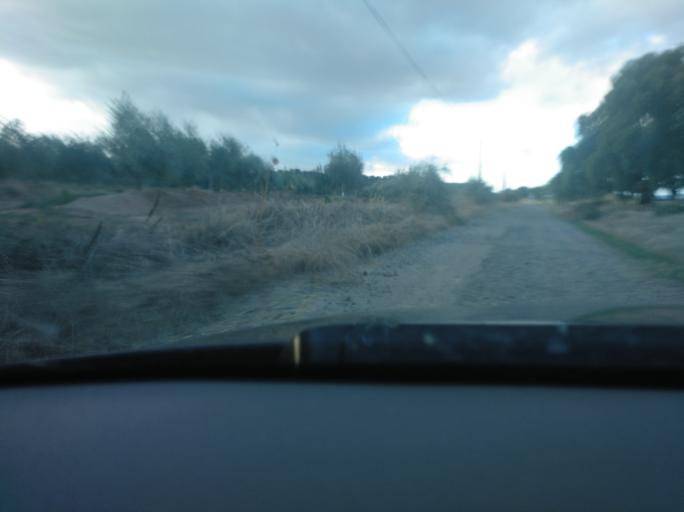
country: PT
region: Portalegre
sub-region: Campo Maior
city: Campo Maior
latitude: 39.0397
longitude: -6.9903
